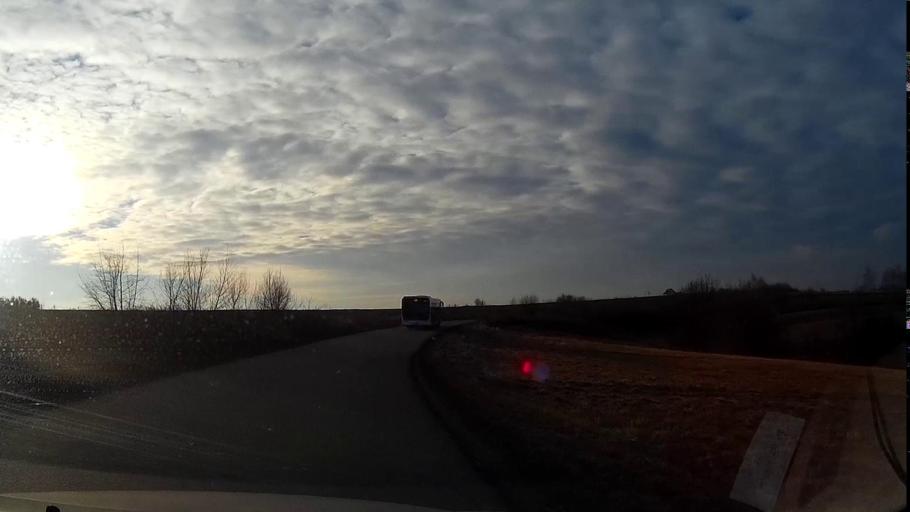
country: PL
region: Lesser Poland Voivodeship
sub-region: Powiat krakowski
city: Sanka
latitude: 50.0619
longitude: 19.6679
